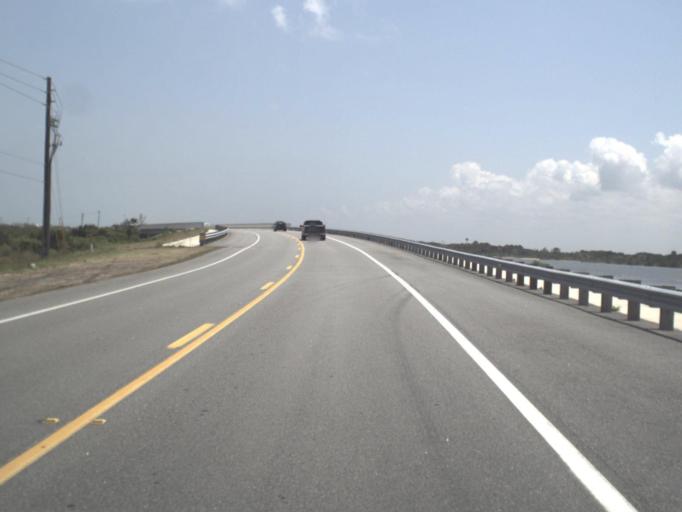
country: US
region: Florida
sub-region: Flagler County
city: Palm Coast
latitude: 29.6822
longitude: -81.2219
